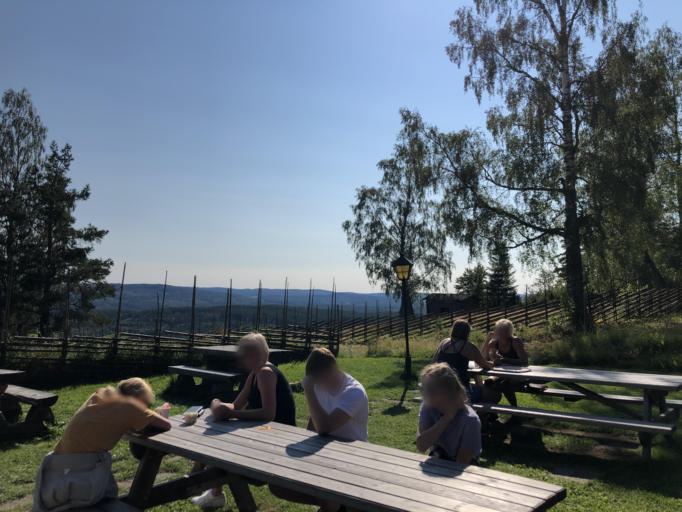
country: SE
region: Dalarna
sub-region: Leksand Municipality
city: Siljansnas
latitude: 60.7883
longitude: 14.8543
